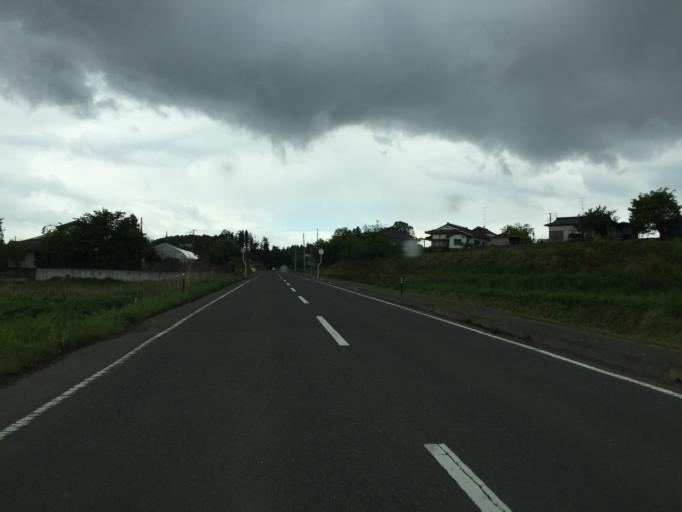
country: JP
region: Fukushima
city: Ishikawa
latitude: 37.1528
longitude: 140.3697
